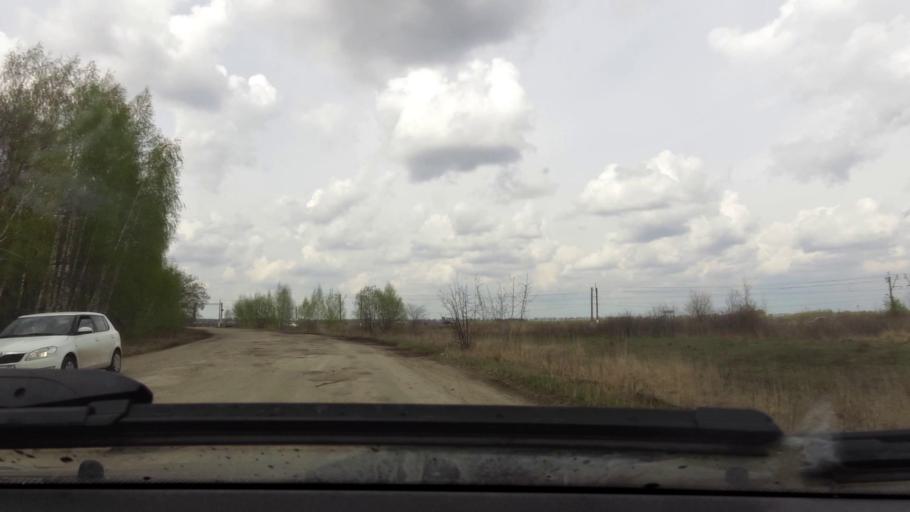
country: RU
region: Rjazan
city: Bagramovo
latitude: 54.7061
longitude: 39.3165
